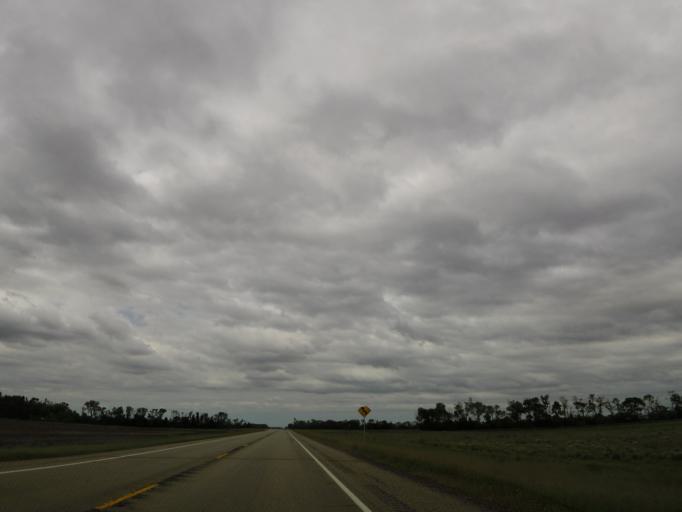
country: US
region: North Dakota
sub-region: Walsh County
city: Grafton
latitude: 48.5330
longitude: -97.4476
